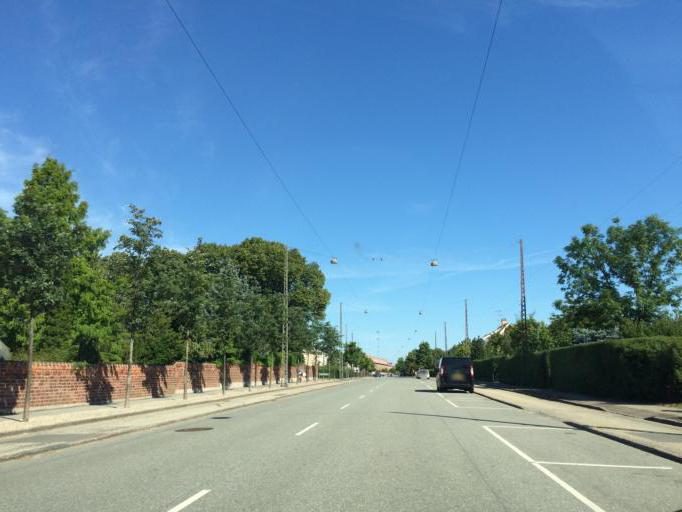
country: DK
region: Capital Region
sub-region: Tarnby Kommune
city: Tarnby
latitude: 55.6322
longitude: 12.6379
